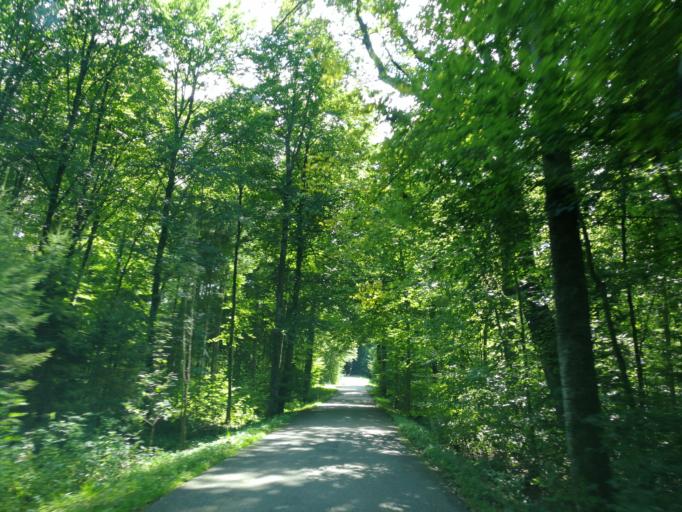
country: CH
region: Thurgau
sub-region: Kreuzlingen District
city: Ermatingen
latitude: 47.6472
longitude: 9.0782
